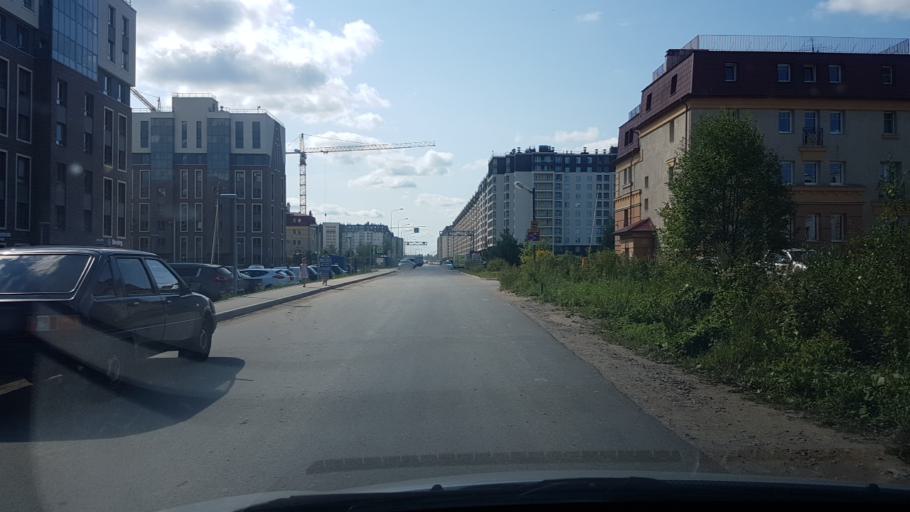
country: RU
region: St.-Petersburg
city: Sosnovaya Polyana
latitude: 59.8457
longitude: 30.1146
